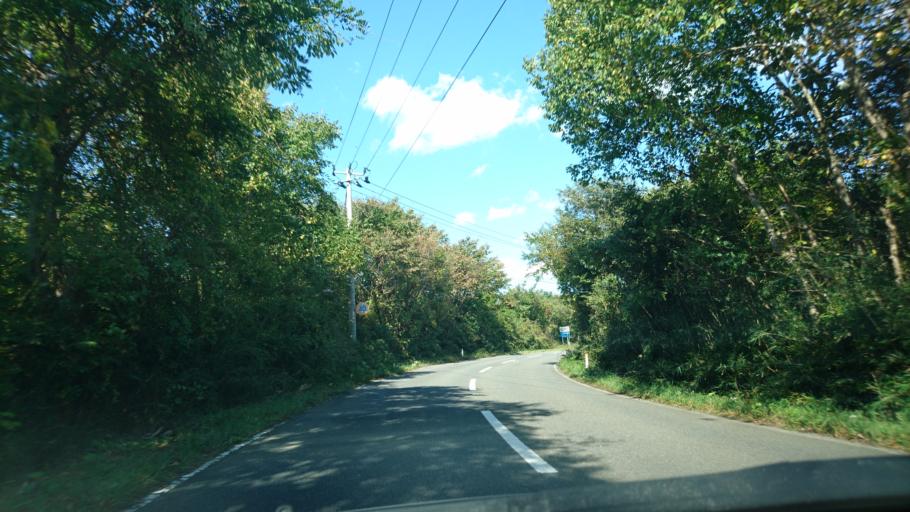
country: JP
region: Iwate
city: Ichinoseki
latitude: 38.8495
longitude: 141.0352
